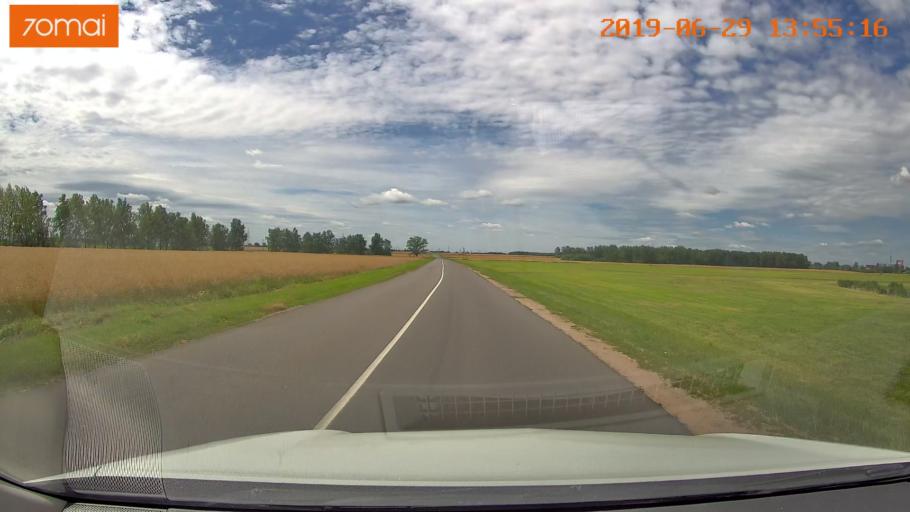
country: BY
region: Minsk
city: Slutsk
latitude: 52.9836
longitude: 27.5230
